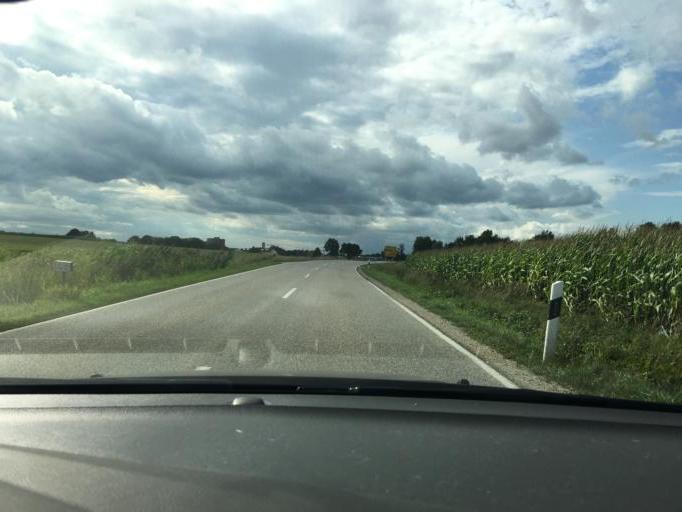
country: DE
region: Bavaria
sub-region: Upper Bavaria
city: Erding
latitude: 48.3012
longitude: 11.9258
